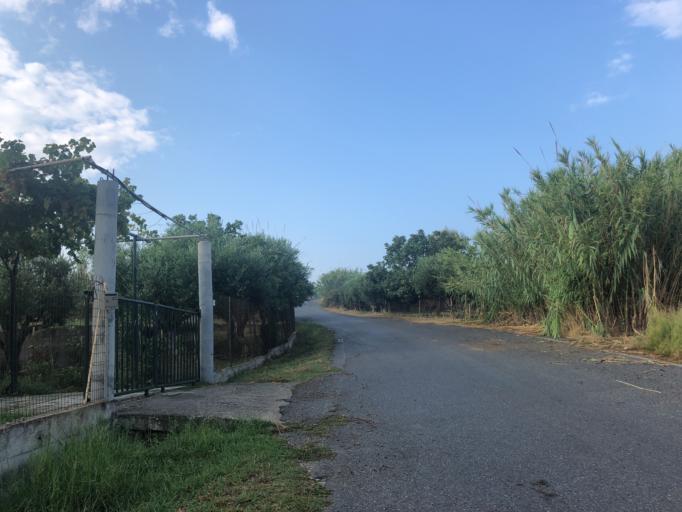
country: GR
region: Crete
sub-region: Nomos Chanias
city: Georgioupolis
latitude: 35.3500
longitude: 24.3147
